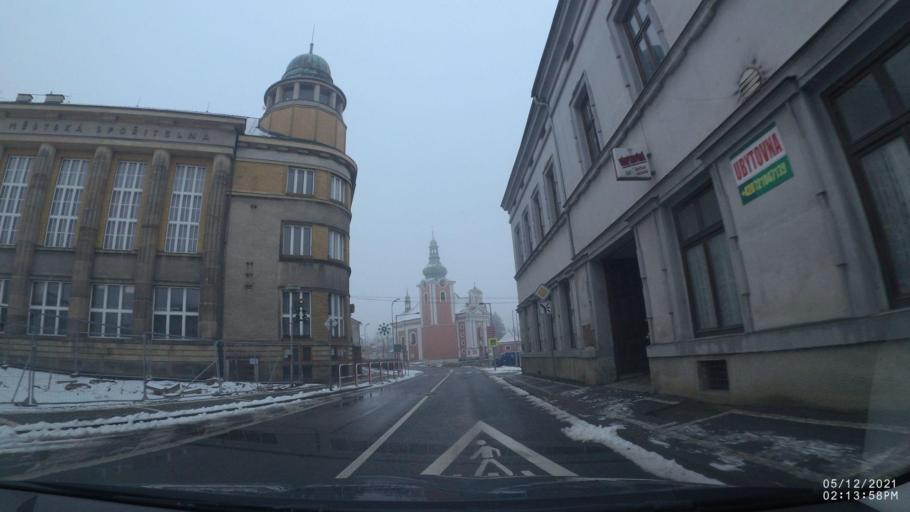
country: CZ
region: Kralovehradecky
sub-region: Okres Nachod
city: Cerveny Kostelec
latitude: 50.4771
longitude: 16.0918
